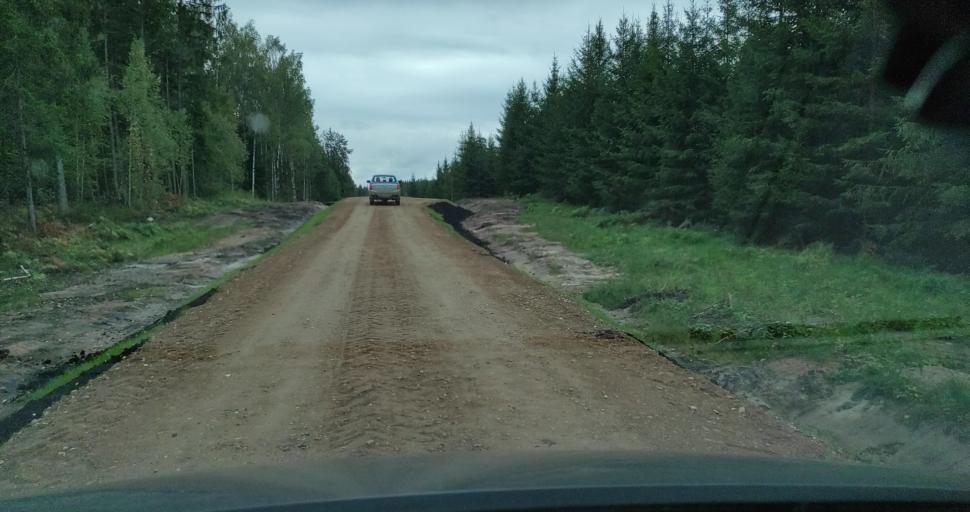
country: LV
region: Talsu Rajons
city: Sabile
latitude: 57.0193
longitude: 22.3532
